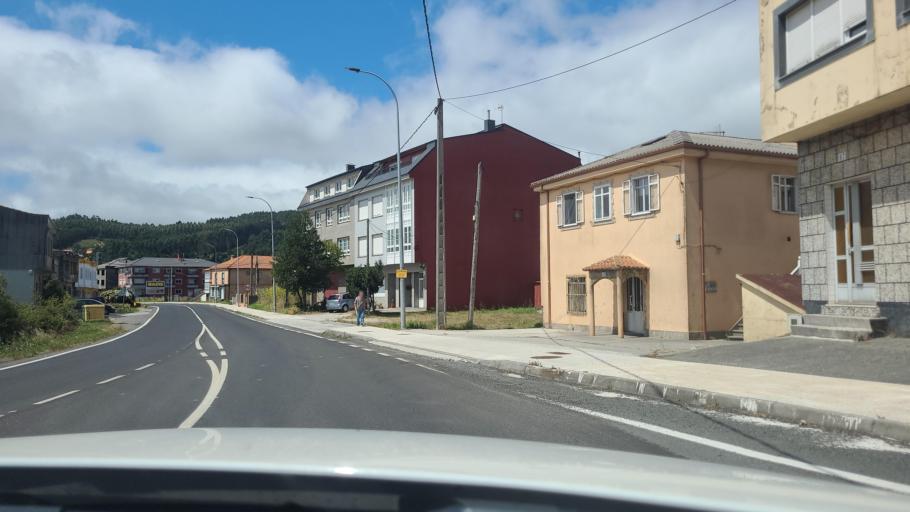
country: ES
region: Galicia
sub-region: Provincia da Coruna
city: Cee
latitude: 42.9467
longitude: -9.1710
